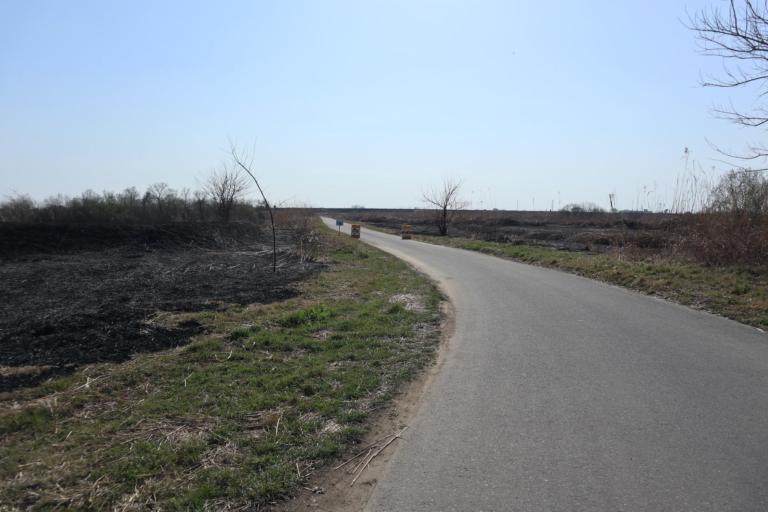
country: JP
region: Tochigi
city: Fujioka
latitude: 36.2585
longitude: 139.6669
